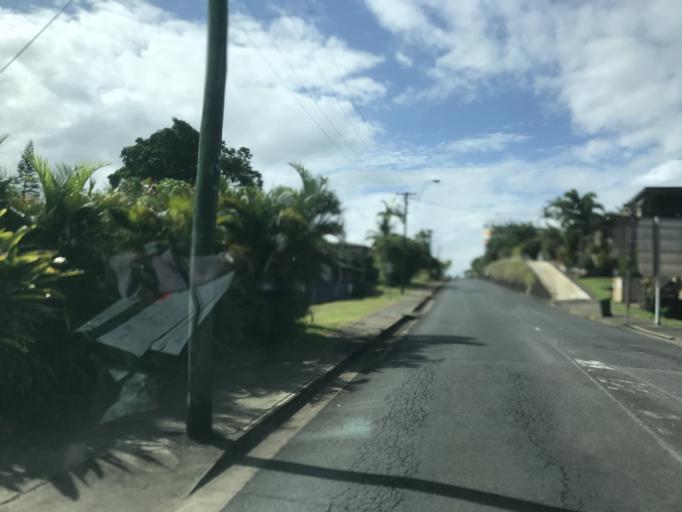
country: AU
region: Queensland
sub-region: Cassowary Coast
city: Innisfail
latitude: -17.5260
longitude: 146.0342
